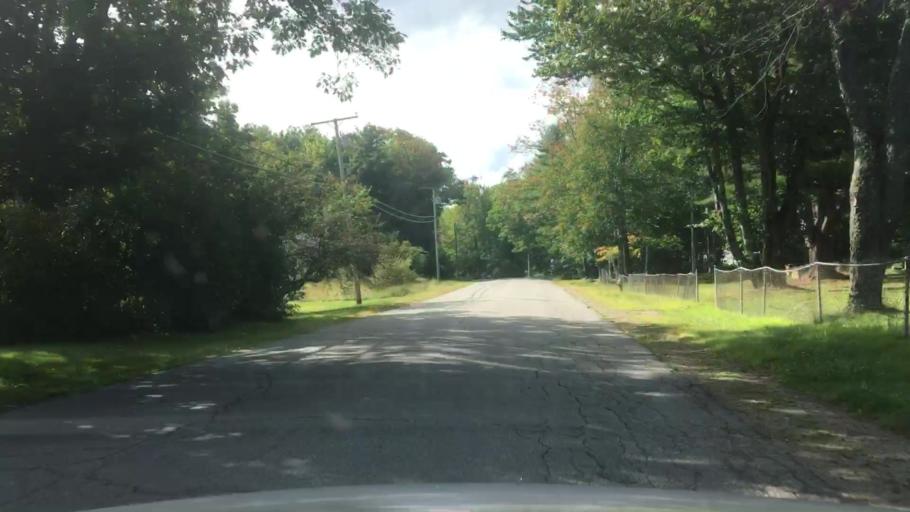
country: US
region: Maine
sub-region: Kennebec County
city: Gardiner
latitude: 44.1802
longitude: -69.8251
